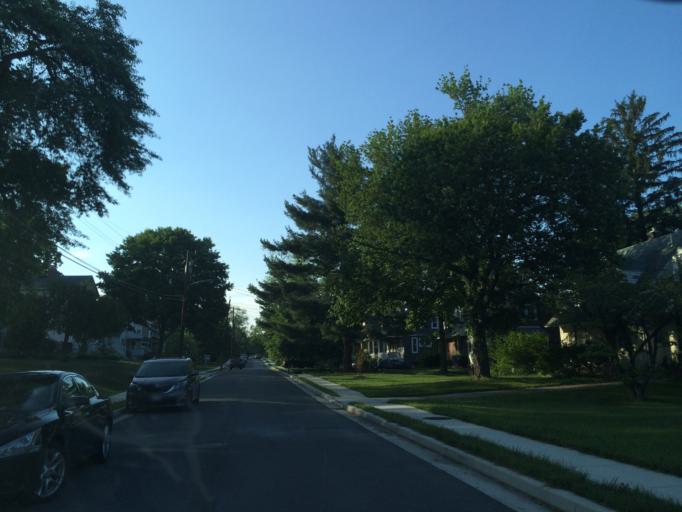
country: US
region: Maryland
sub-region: Baltimore County
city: Catonsville
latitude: 39.2665
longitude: -76.7366
